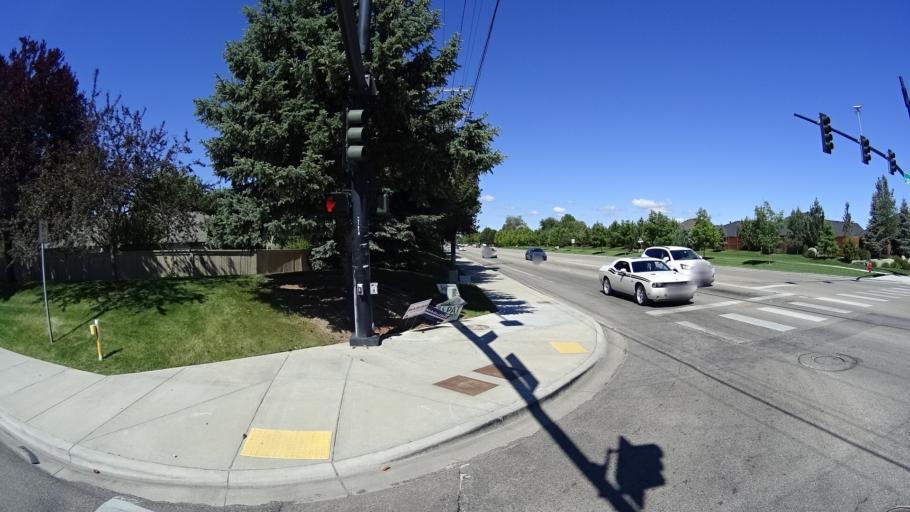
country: US
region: Idaho
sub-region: Ada County
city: Meridian
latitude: 43.6337
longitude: -116.3747
